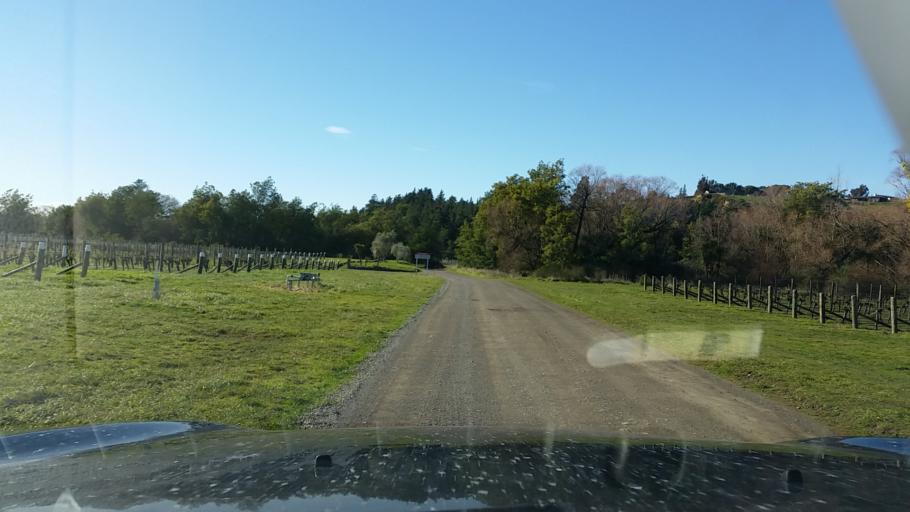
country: NZ
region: Marlborough
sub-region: Marlborough District
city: Blenheim
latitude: -41.5298
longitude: 173.7998
